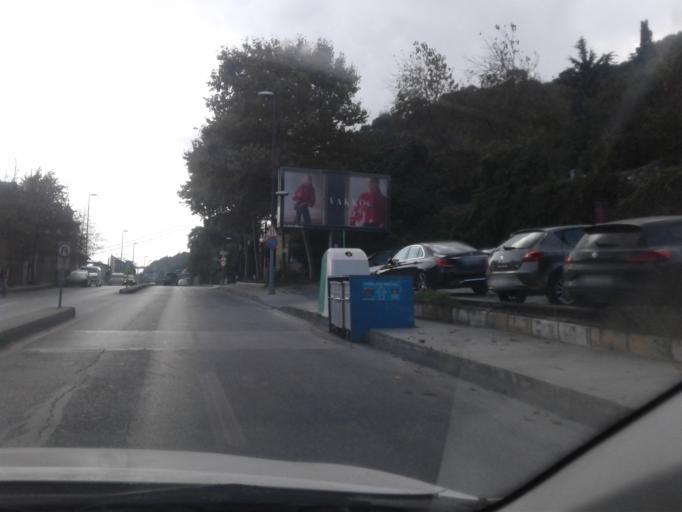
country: TR
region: Istanbul
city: UEskuedar
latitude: 41.0589
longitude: 29.0356
